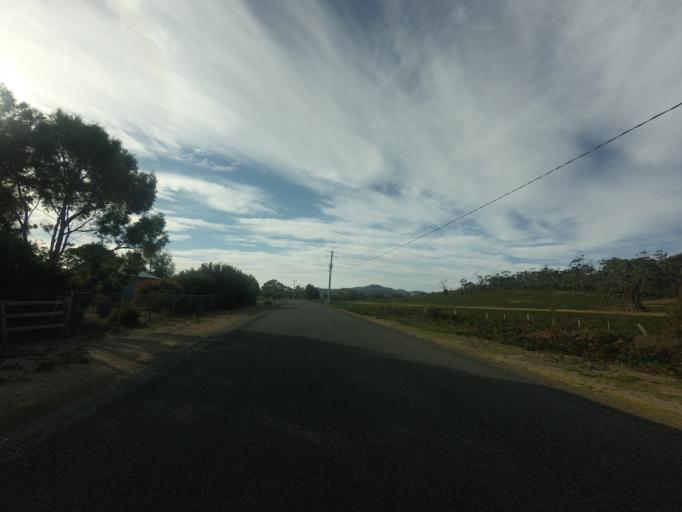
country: AU
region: Tasmania
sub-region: Sorell
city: Sorell
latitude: -42.9682
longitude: 147.8318
